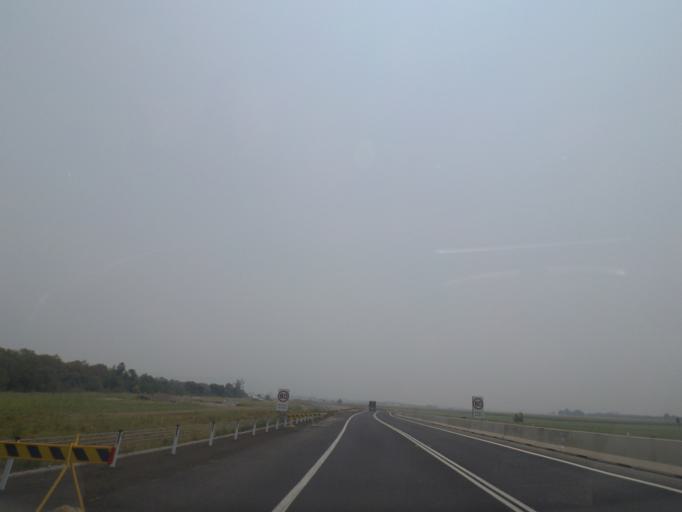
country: AU
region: New South Wales
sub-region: Clarence Valley
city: Maclean
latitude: -29.4040
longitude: 153.2424
